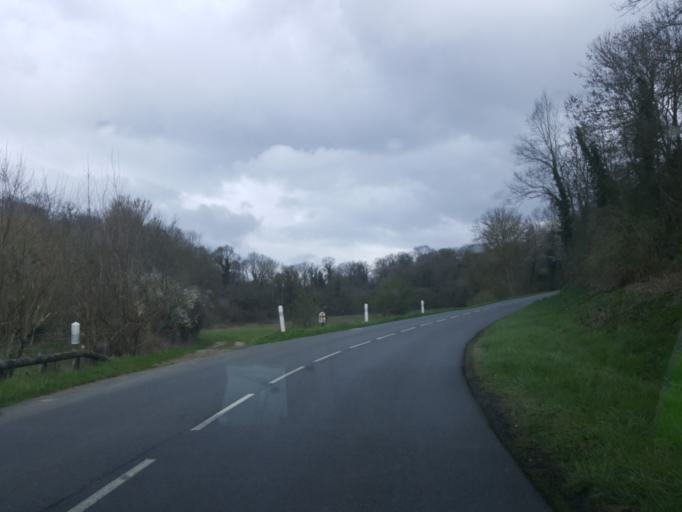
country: FR
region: Ile-de-France
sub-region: Departement du Val-d'Oise
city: Magny-en-Vexin
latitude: 49.1729
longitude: 1.7811
